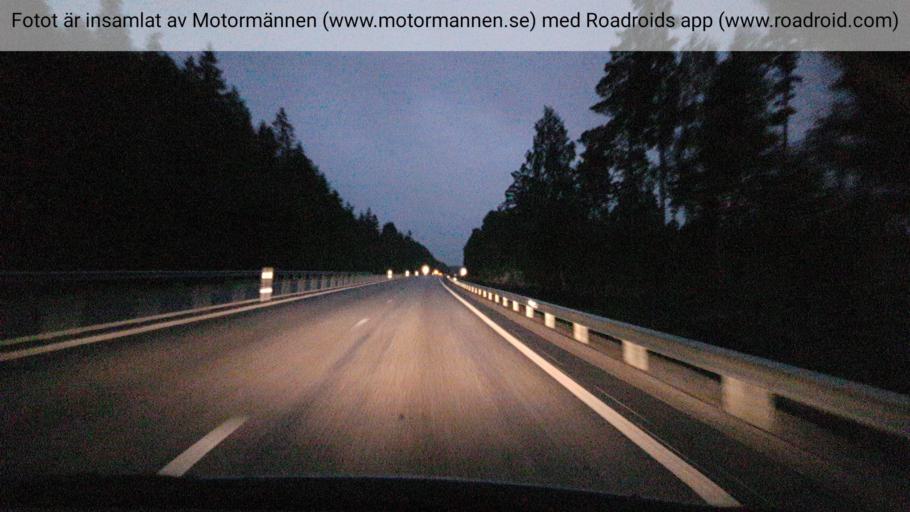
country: SE
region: Vaestmanland
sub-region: Surahammars Kommun
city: Surahammar
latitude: 59.7081
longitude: 16.2460
